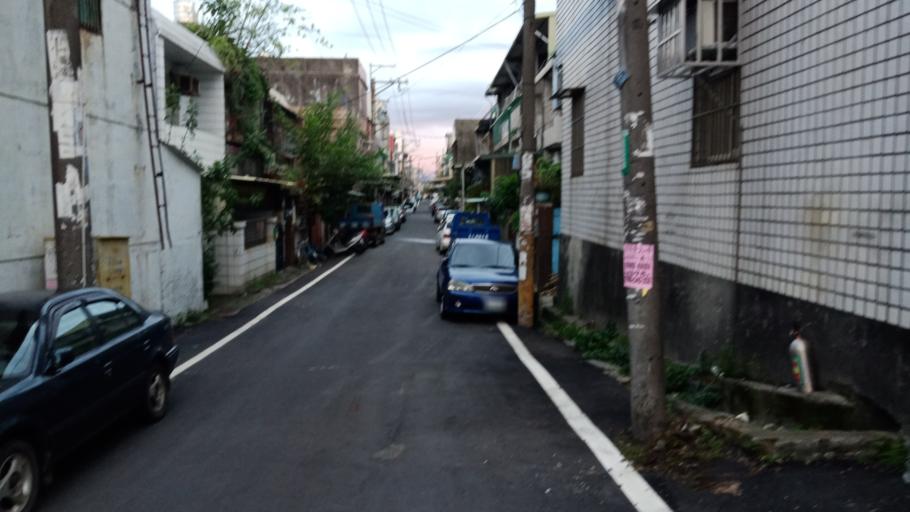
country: TW
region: Taiwan
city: Daxi
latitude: 24.8725
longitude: 121.1971
